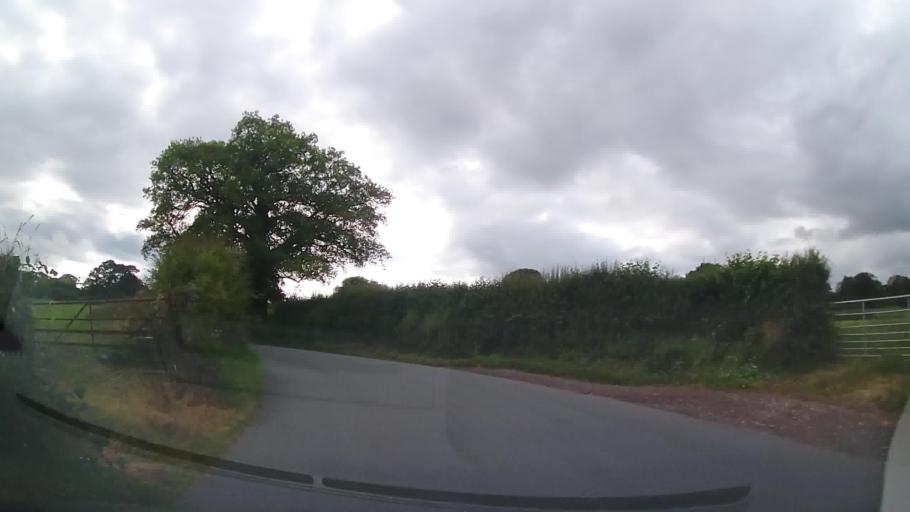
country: GB
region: England
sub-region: Shropshire
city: Wem
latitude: 52.9039
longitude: -2.7122
